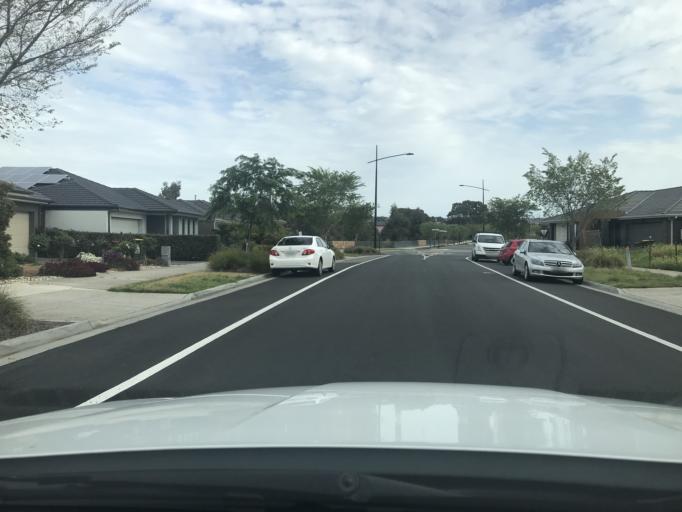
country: AU
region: Victoria
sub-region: Hume
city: Roxburgh Park
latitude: -37.5943
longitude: 144.8993
